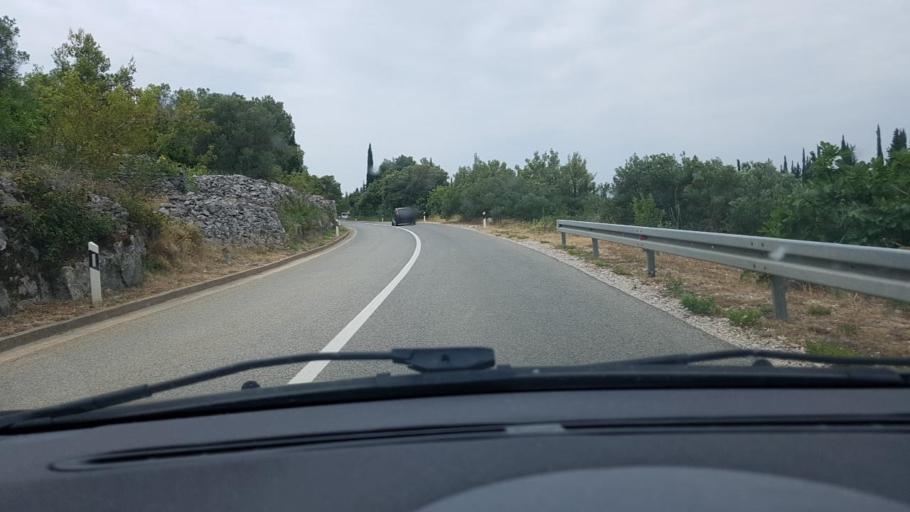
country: HR
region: Dubrovacko-Neretvanska
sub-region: Grad Korcula
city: Zrnovo
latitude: 42.9378
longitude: 17.0967
